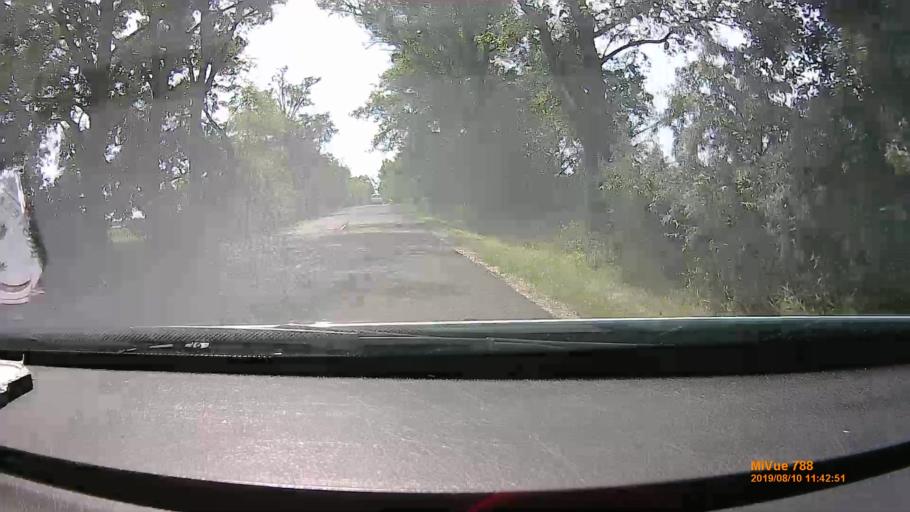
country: HU
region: Borsod-Abauj-Zemplen
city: Szentistvan
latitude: 47.7363
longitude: 20.6163
